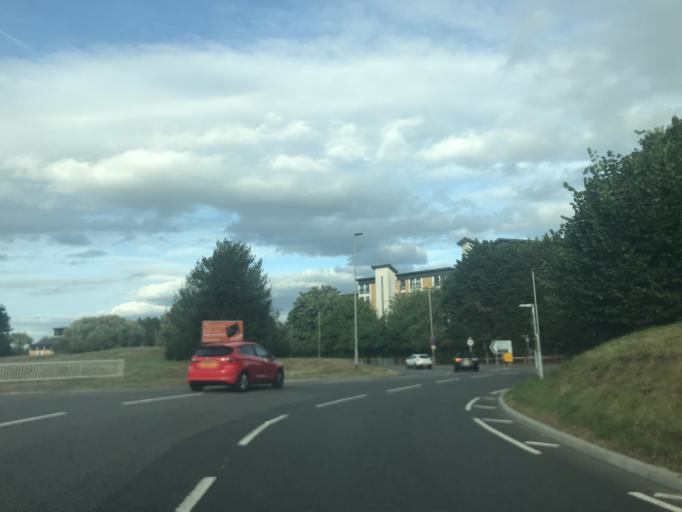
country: GB
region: England
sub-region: Bracknell Forest
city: Bracknell
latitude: 51.4131
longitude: -0.7502
